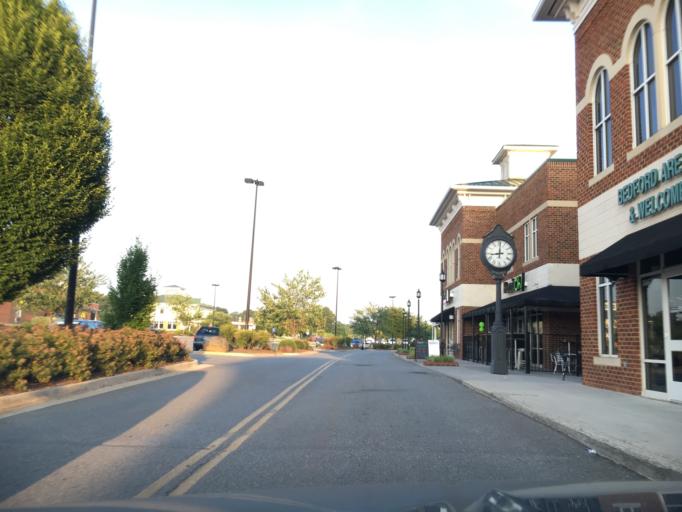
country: US
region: Virginia
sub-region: Bedford County
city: Forest
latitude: 37.3657
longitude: -79.2967
